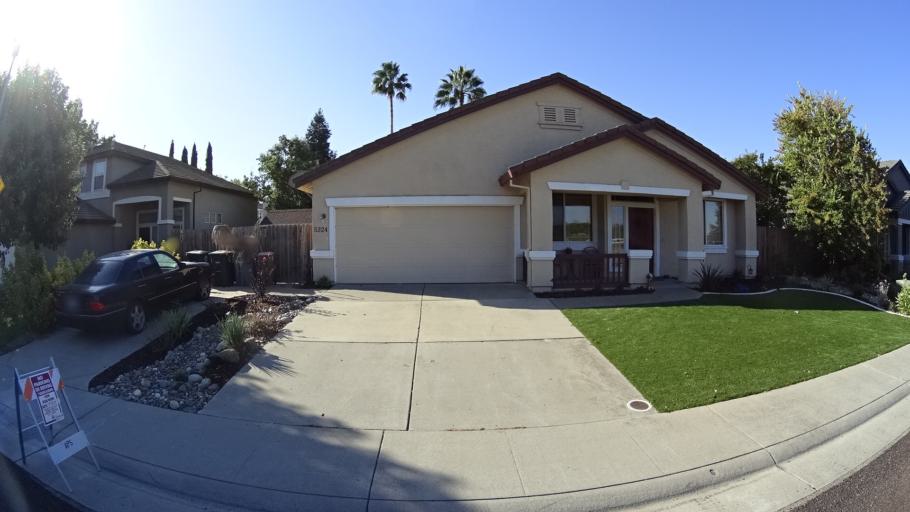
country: US
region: California
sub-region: Sacramento County
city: Laguna
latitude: 38.4251
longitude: -121.4419
